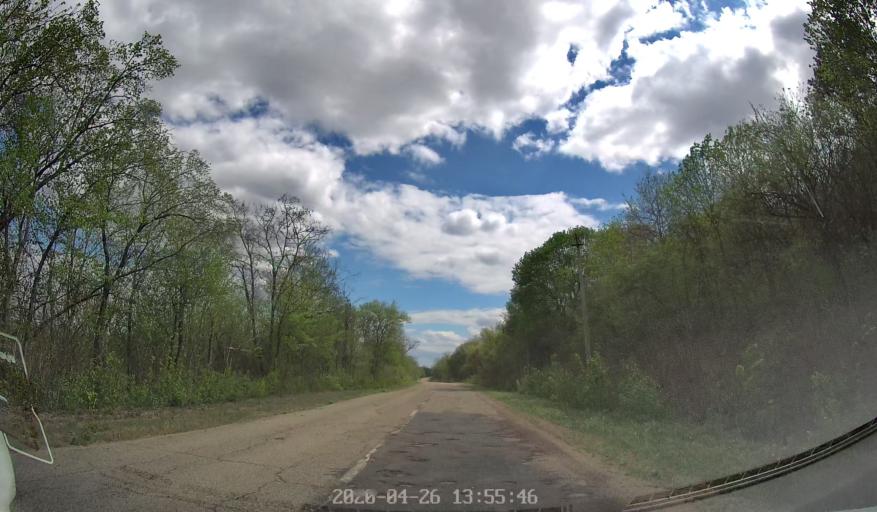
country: MD
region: Telenesti
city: Cocieri
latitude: 47.2837
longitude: 29.1031
